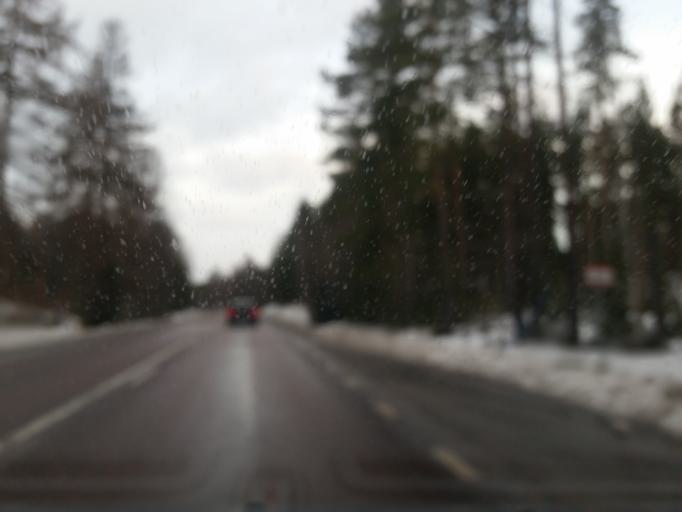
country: SE
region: Gaevleborg
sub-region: Sandvikens Kommun
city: Jarbo
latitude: 60.6900
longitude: 16.6409
